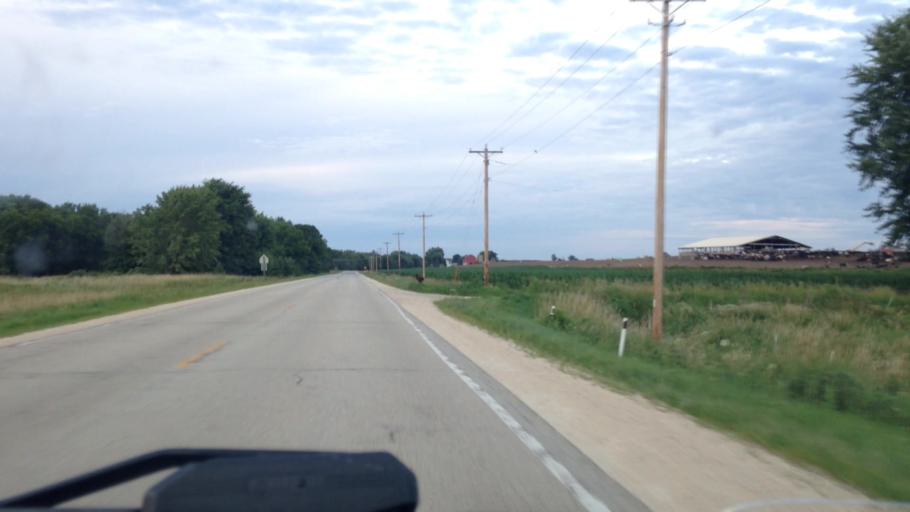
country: US
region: Wisconsin
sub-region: Dodge County
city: Mayville
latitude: 43.4870
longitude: -88.4970
